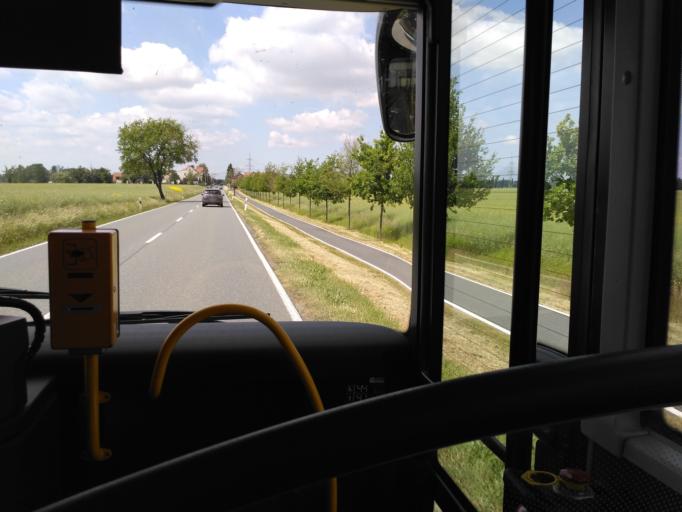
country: DE
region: Saxony
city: Strehla
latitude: 51.3340
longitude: 13.2598
